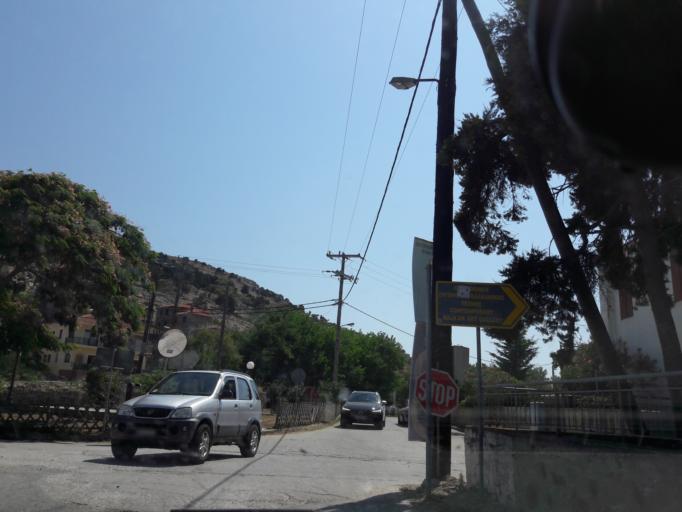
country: GR
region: North Aegean
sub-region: Nomos Lesvou
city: Myrina
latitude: 39.8642
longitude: 25.1510
